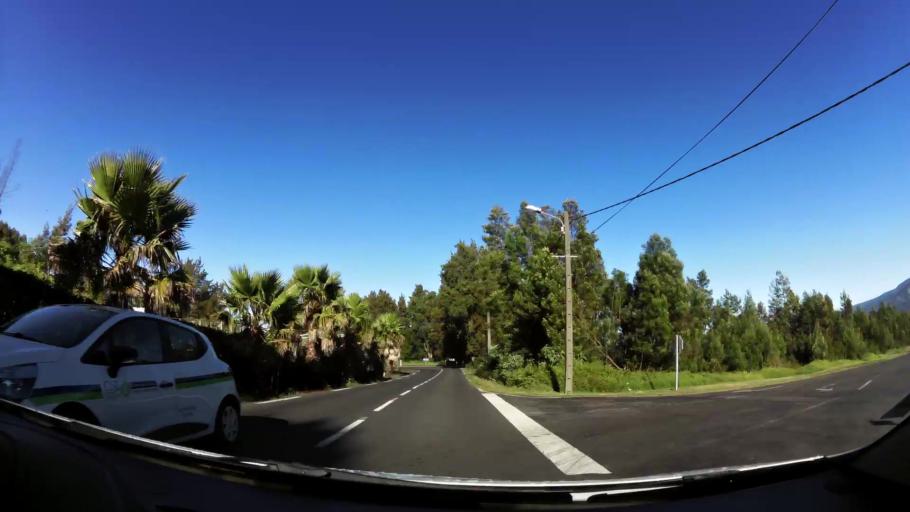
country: RE
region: Reunion
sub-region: Reunion
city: Le Tampon
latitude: -21.2190
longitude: 55.5602
